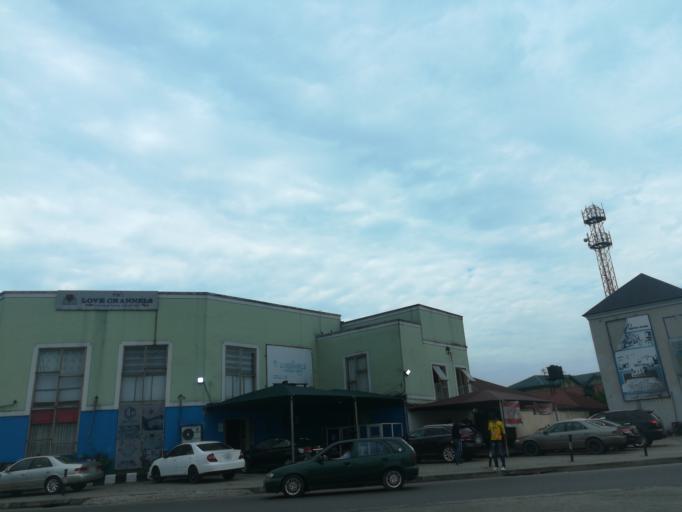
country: NG
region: Rivers
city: Port Harcourt
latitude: 4.8354
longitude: 6.9773
